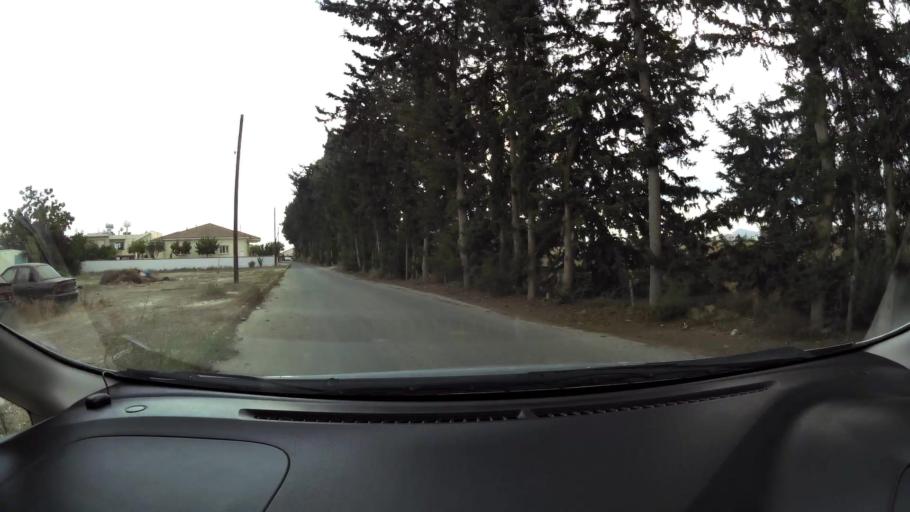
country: CY
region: Larnaka
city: Meneou
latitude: 34.8643
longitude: 33.5968
